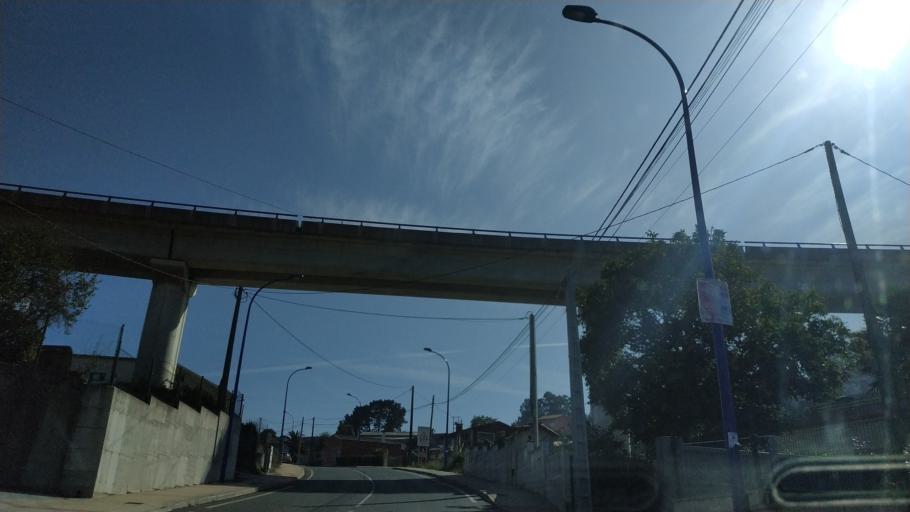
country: ES
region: Galicia
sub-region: Provincia da Coruna
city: Culleredo
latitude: 43.3037
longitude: -8.3845
